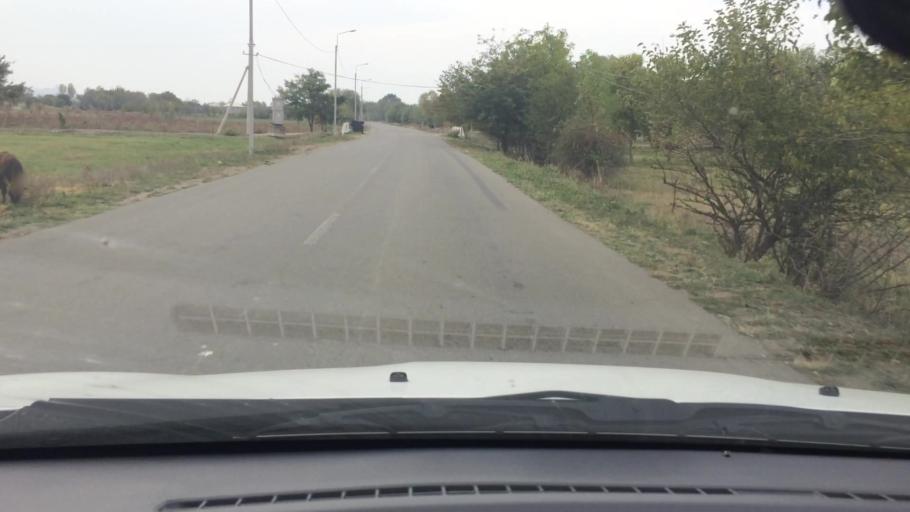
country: AM
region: Tavush
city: Berdavan
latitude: 41.3478
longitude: 44.9778
